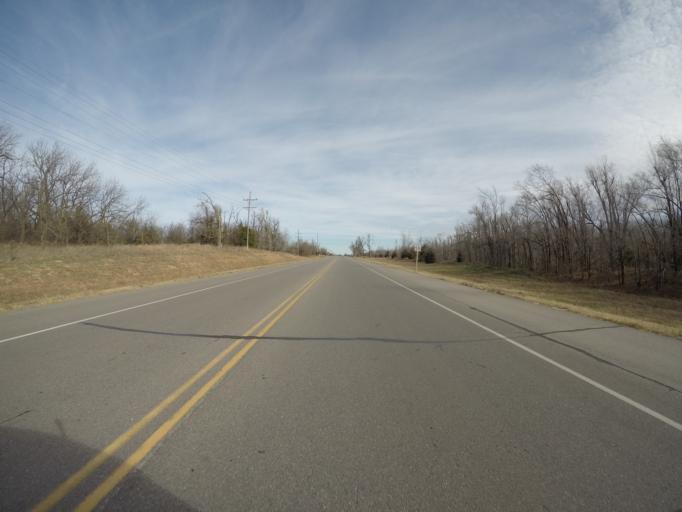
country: US
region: Kansas
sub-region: Reno County
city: Hutchinson
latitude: 38.1015
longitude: -97.8709
